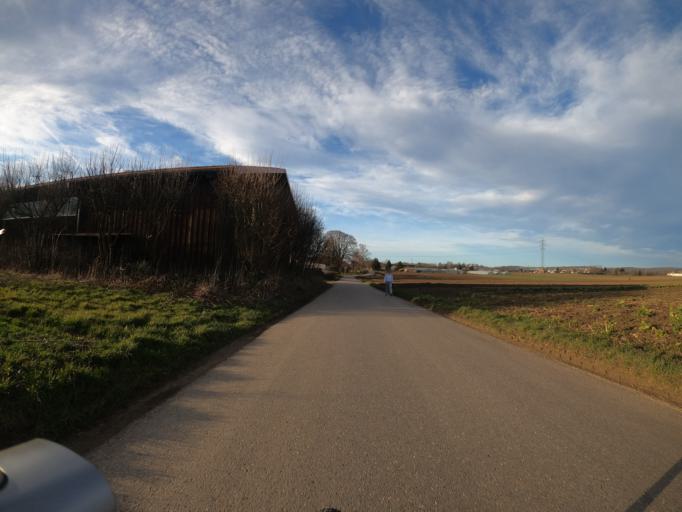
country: DE
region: Baden-Wuerttemberg
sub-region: Regierungsbezirk Stuttgart
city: Denkendorf
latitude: 48.7057
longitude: 9.3170
